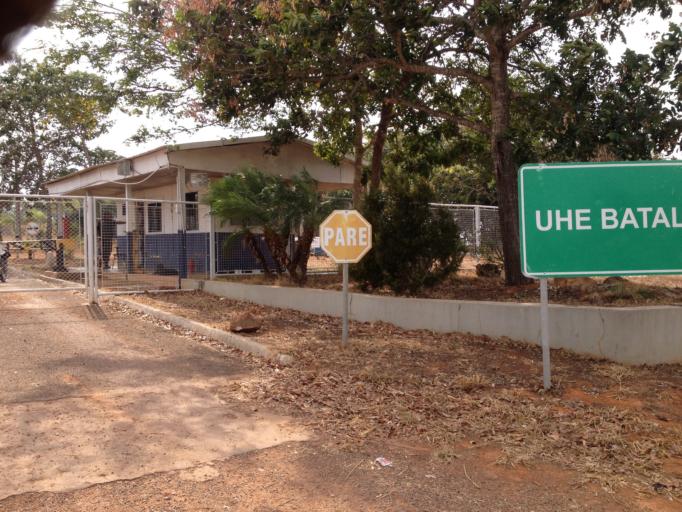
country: BR
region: Goias
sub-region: Cristalina
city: Cristalina
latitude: -17.3545
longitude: -47.4979
